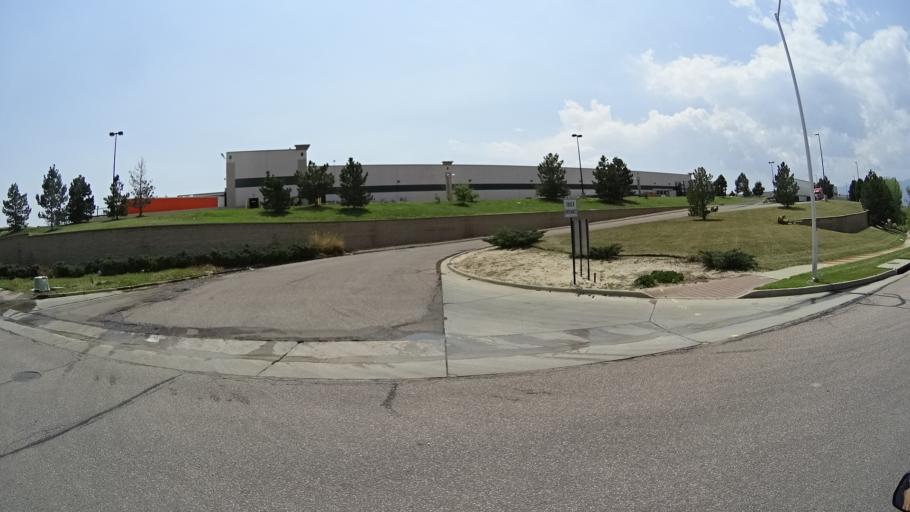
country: US
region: Colorado
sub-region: El Paso County
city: Black Forest
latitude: 38.9448
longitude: -104.7235
